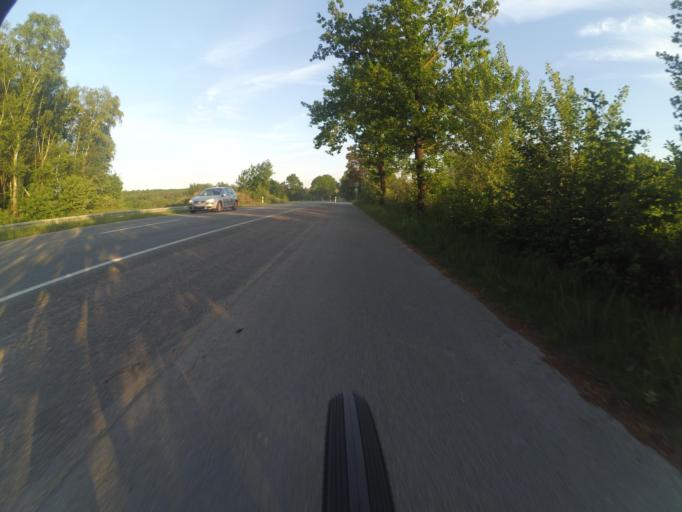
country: DE
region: North Rhine-Westphalia
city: Ibbenburen
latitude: 52.3235
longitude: 7.6701
